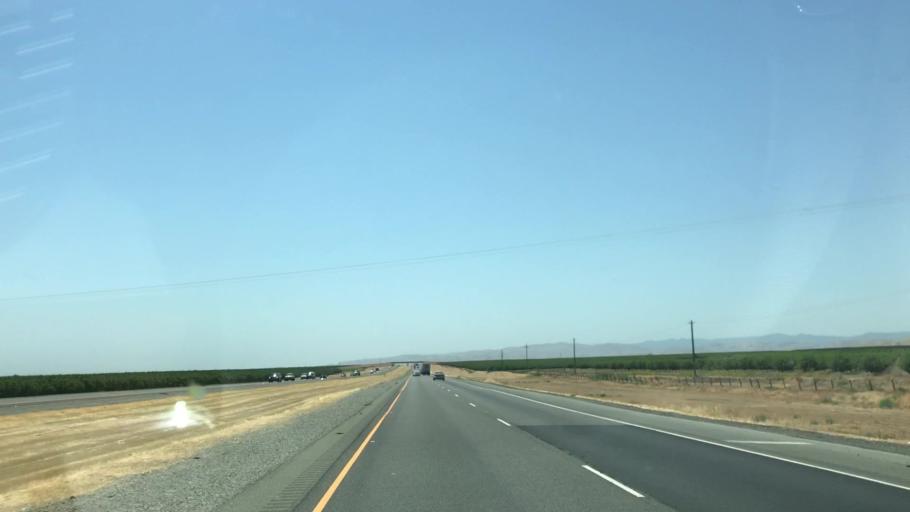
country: US
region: California
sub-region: Merced County
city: South Dos Palos
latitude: 36.7362
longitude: -120.6957
